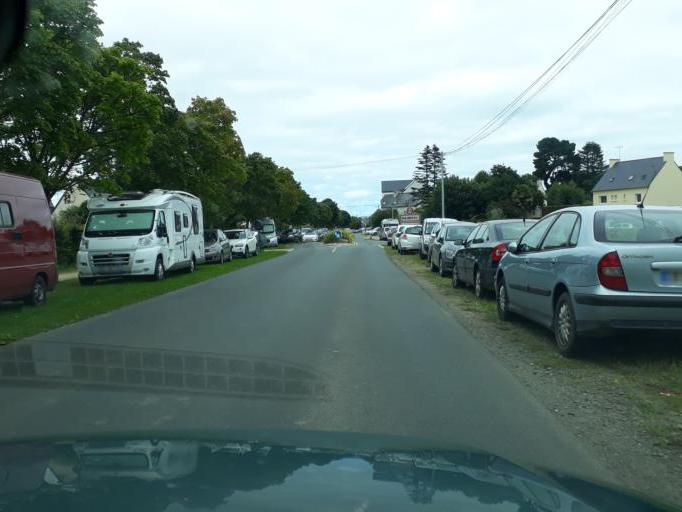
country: FR
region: Brittany
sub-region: Departement des Cotes-d'Armor
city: Paimpol
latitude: 48.7732
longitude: -3.0563
